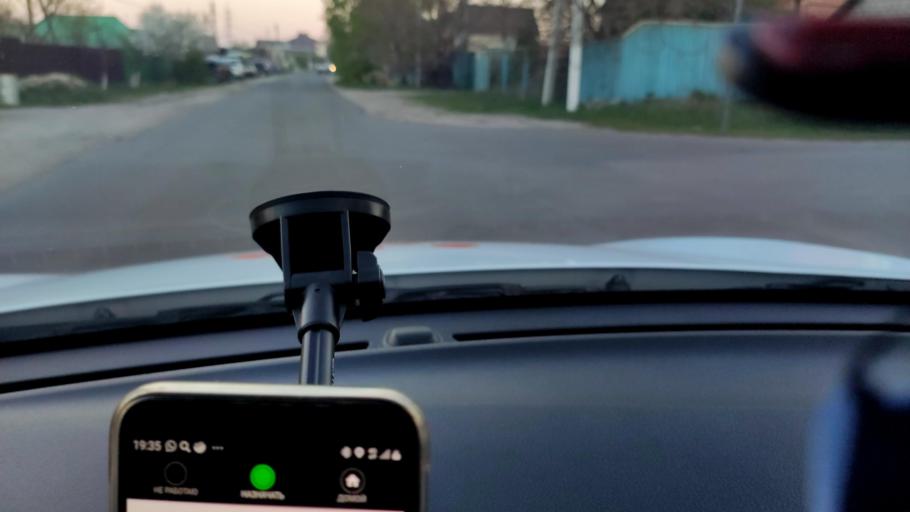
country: RU
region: Voronezj
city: Somovo
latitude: 51.6807
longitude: 39.3293
